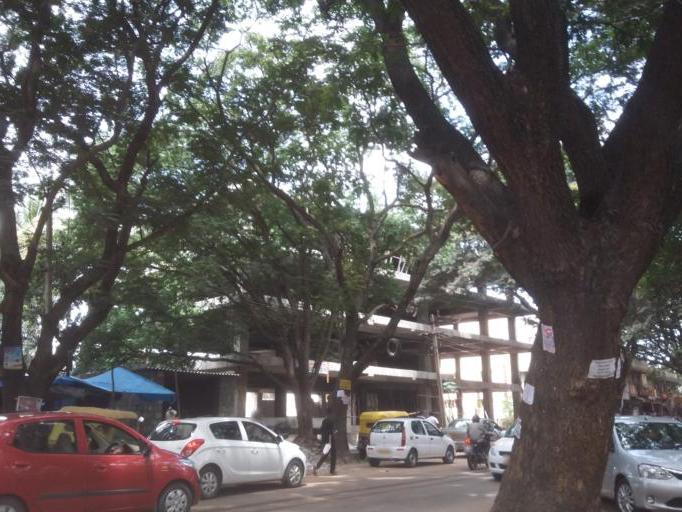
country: IN
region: Karnataka
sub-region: Bangalore Urban
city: Bangalore
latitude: 12.9536
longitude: 77.6529
